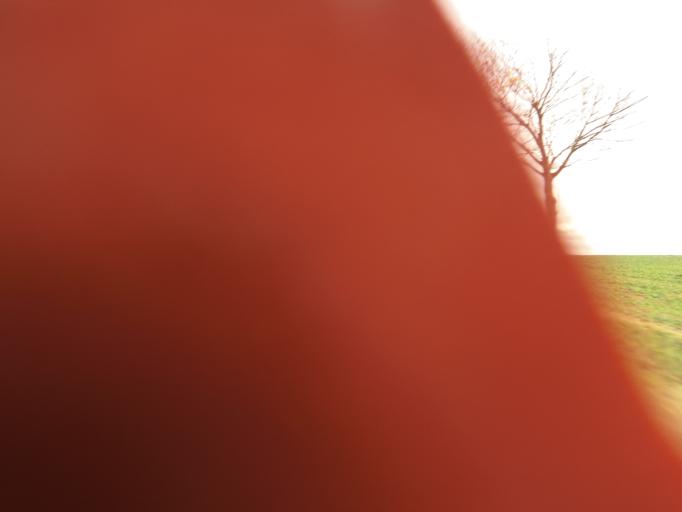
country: DE
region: Saxony-Anhalt
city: Droyssig
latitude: 51.0741
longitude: 12.0186
